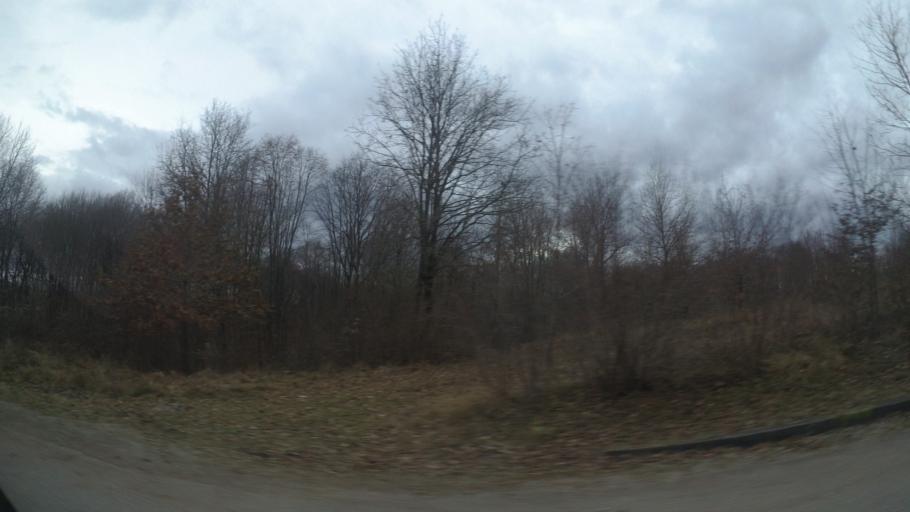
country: HR
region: Karlovacka
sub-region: Grad Karlovac
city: Karlovac
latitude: 45.3702
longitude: 15.5558
